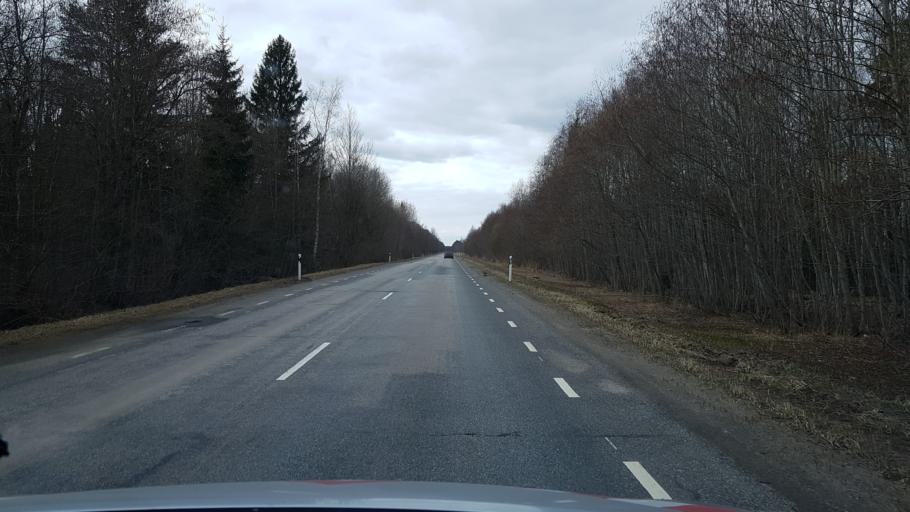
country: EE
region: Ida-Virumaa
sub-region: Narva linn
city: Narva
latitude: 59.3532
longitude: 28.0890
